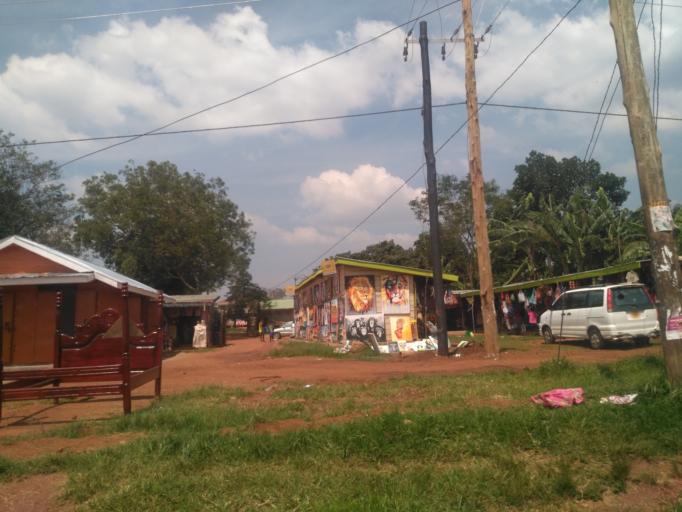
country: UG
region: Central Region
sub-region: Wakiso District
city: Entebbe
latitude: 0.0669
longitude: 32.4755
